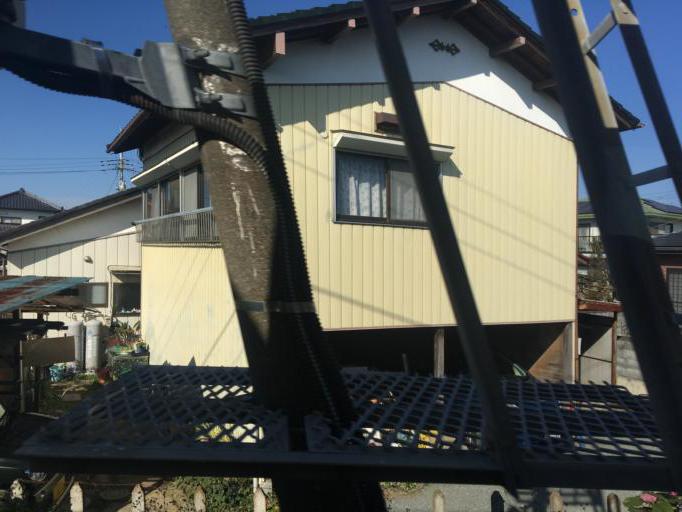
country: JP
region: Gunma
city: Isesaki
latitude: 36.3557
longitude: 139.2383
